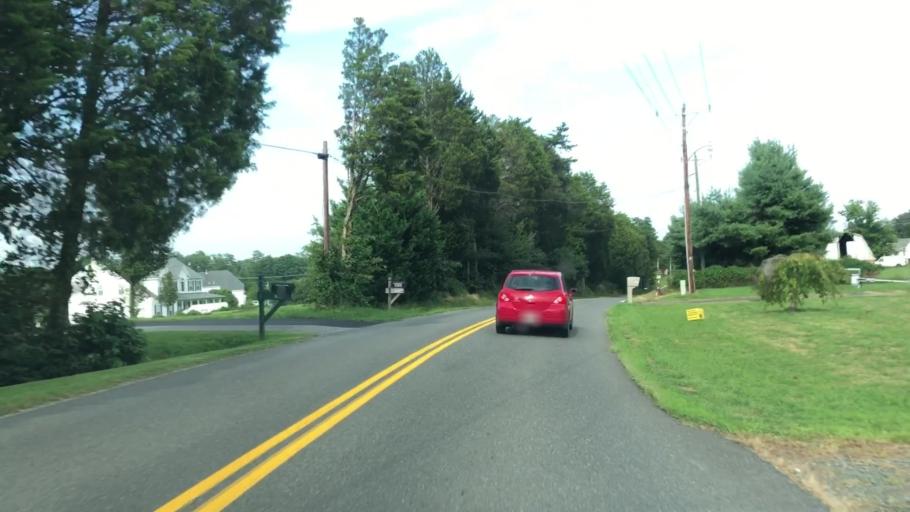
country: US
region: Virginia
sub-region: Stafford County
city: Stafford
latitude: 38.4222
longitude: -77.4800
